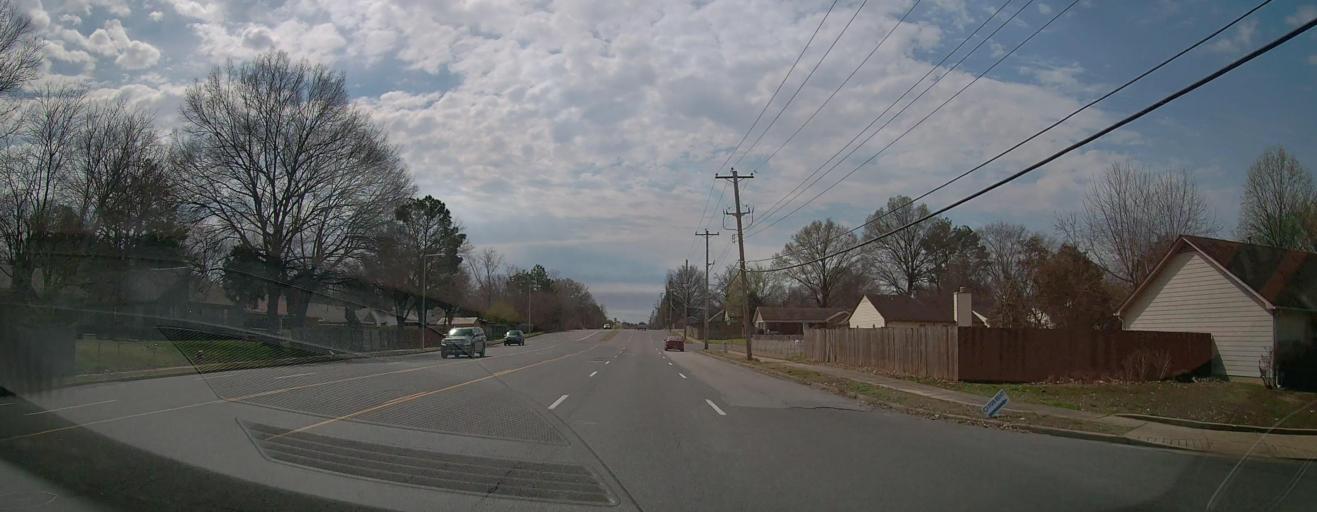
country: US
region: Tennessee
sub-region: Shelby County
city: Germantown
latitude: 35.0311
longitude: -89.8482
